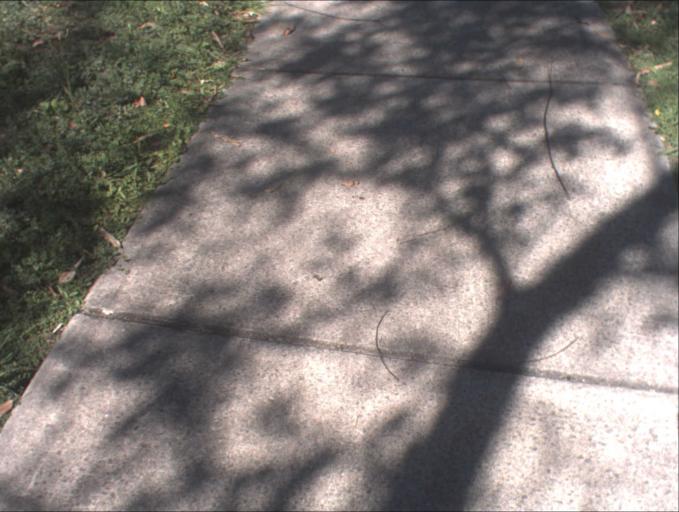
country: AU
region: Queensland
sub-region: Logan
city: Windaroo
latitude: -27.7226
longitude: 153.1708
